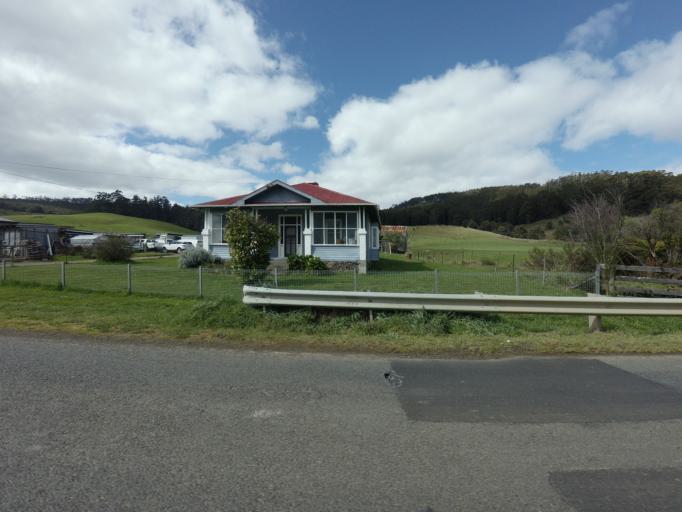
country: AU
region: Tasmania
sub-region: Huon Valley
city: Cygnet
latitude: -43.2922
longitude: 147.0111
